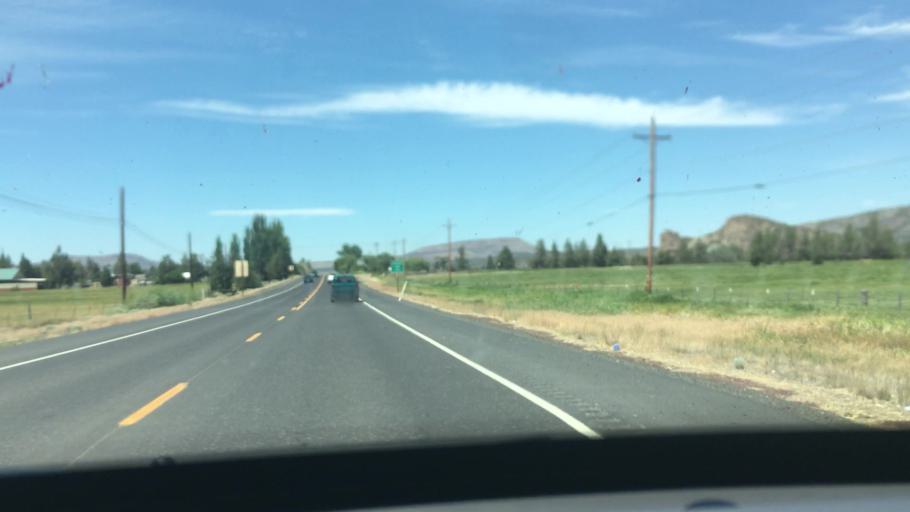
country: US
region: Oregon
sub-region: Deschutes County
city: Terrebonne
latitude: 44.3673
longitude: -121.1785
